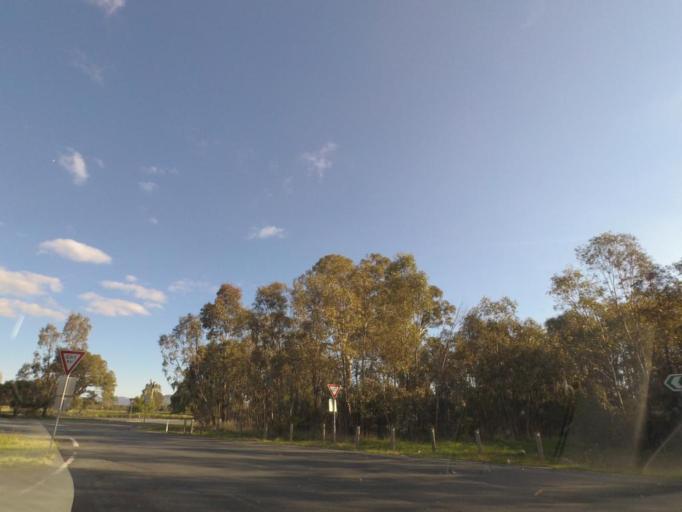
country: AU
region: Victoria
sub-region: Benalla
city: Benalla
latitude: -36.6963
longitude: 145.6586
